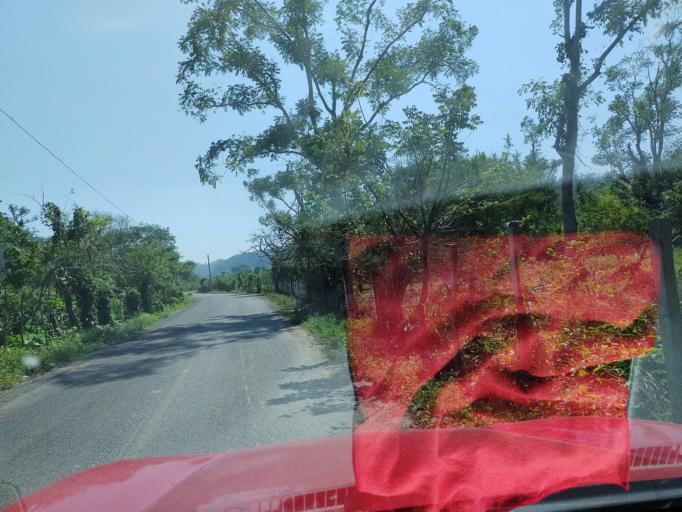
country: MX
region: Veracruz
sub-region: Papantla
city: Polutla
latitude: 20.4995
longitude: -97.2136
